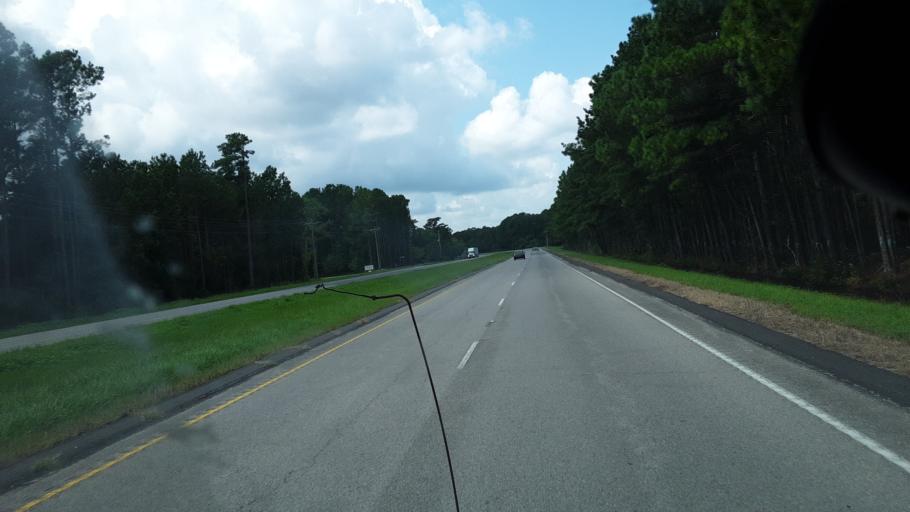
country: US
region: South Carolina
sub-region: Charleston County
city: Awendaw
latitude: 33.0381
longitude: -79.6107
